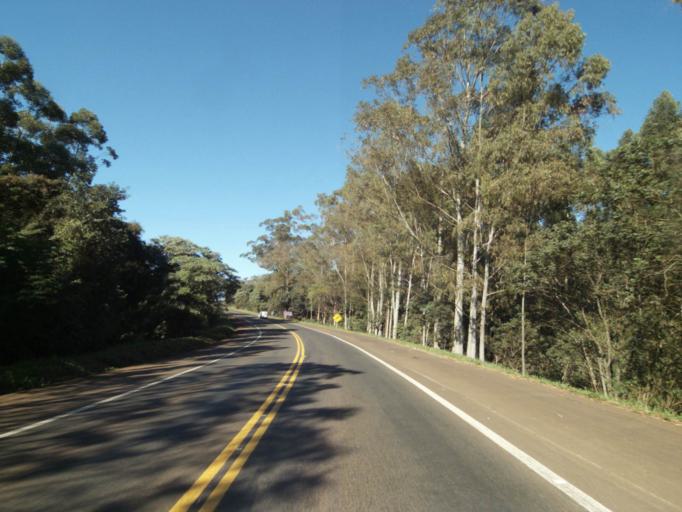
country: BR
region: Parana
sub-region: Faxinal
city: Faxinal
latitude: -23.7458
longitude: -51.1305
